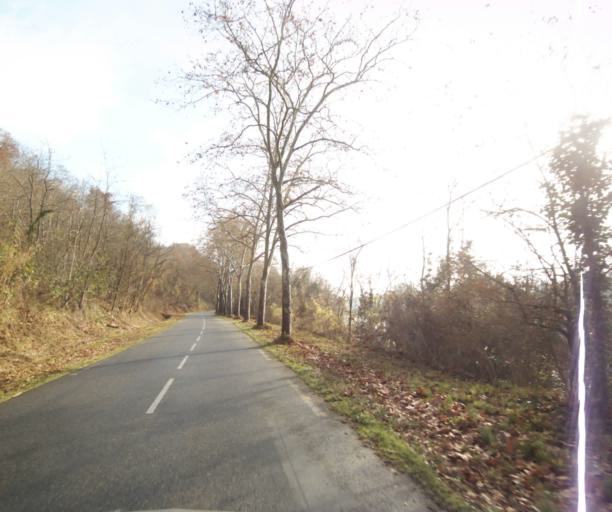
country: FR
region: Midi-Pyrenees
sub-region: Departement de la Haute-Garonne
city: Villemur-sur-Tarn
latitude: 43.8555
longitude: 1.5135
